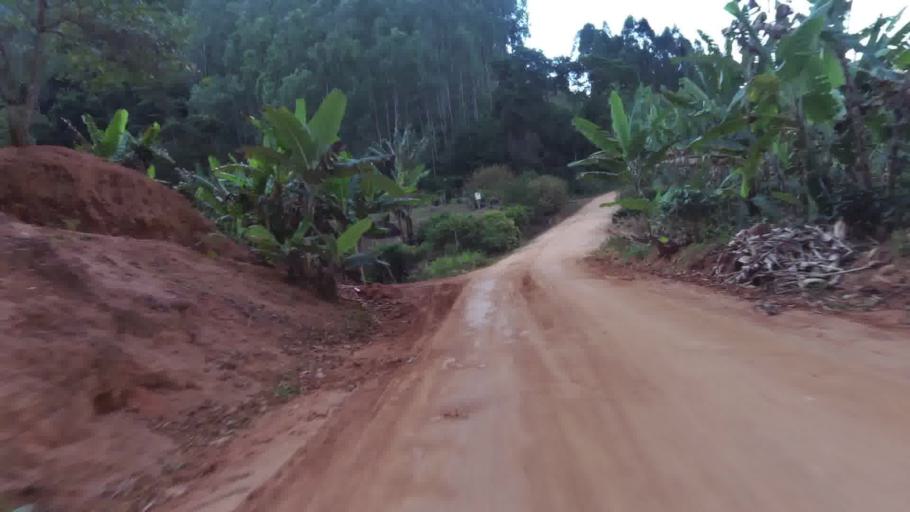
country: BR
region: Espirito Santo
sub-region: Alfredo Chaves
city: Alfredo Chaves
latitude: -20.5538
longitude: -40.6898
